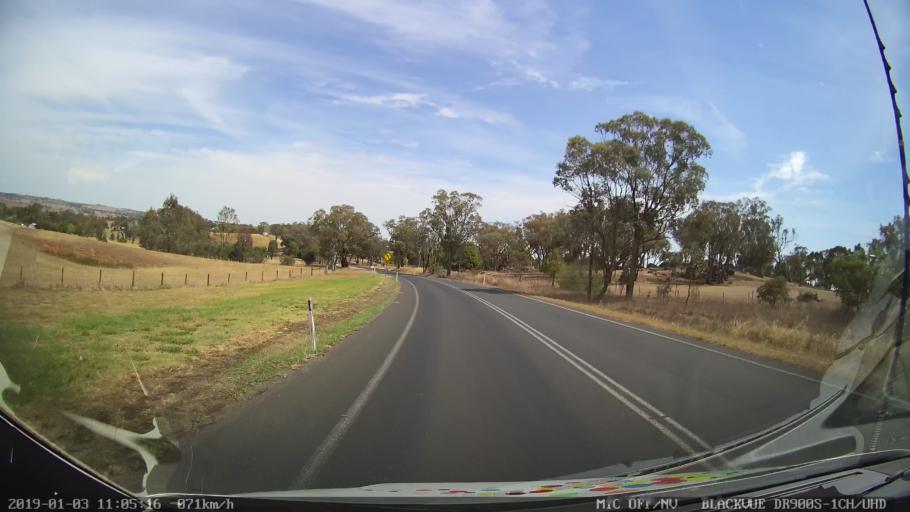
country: AU
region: New South Wales
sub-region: Young
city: Young
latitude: -34.2732
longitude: 148.2863
